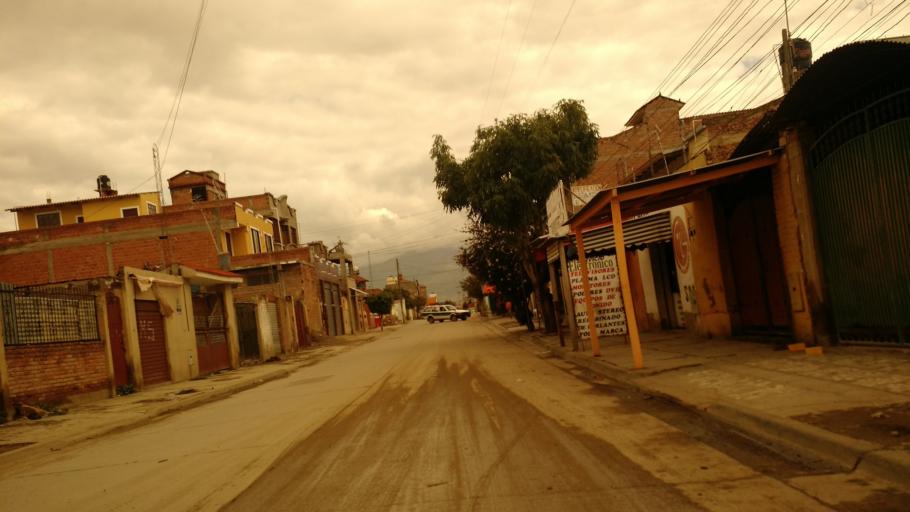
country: BO
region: Cochabamba
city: Cochabamba
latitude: -17.4378
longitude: -66.1564
